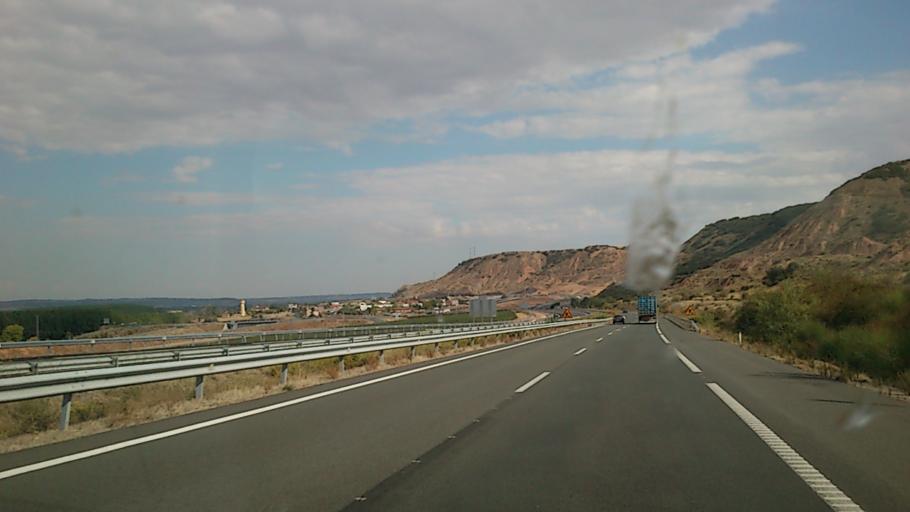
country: ES
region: La Rioja
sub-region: Provincia de La Rioja
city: Murillo de Rio Leza
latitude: 42.4487
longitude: -2.3571
